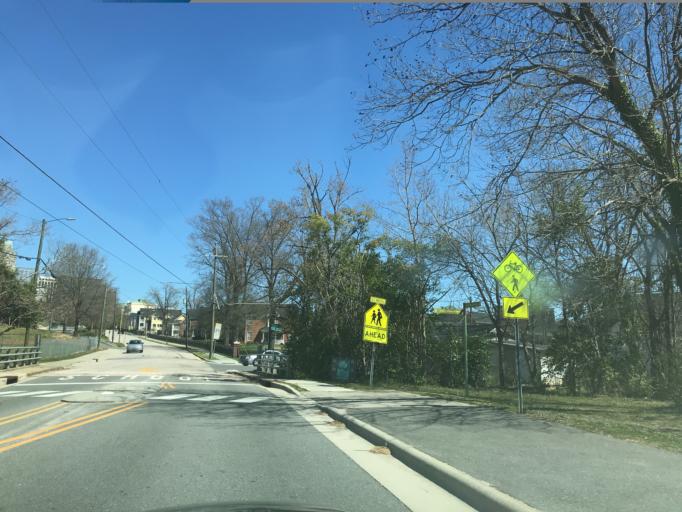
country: US
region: North Carolina
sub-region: Wake County
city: Raleigh
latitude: 35.7655
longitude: -78.6432
